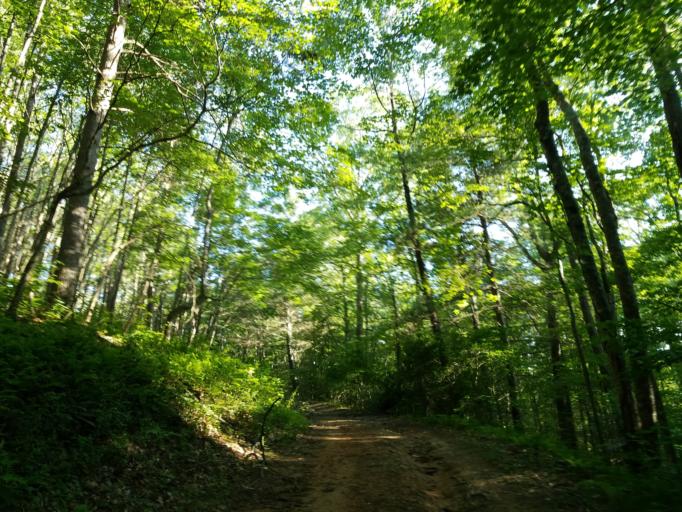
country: US
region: Georgia
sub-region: Fannin County
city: Blue Ridge
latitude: 34.8075
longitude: -84.1664
